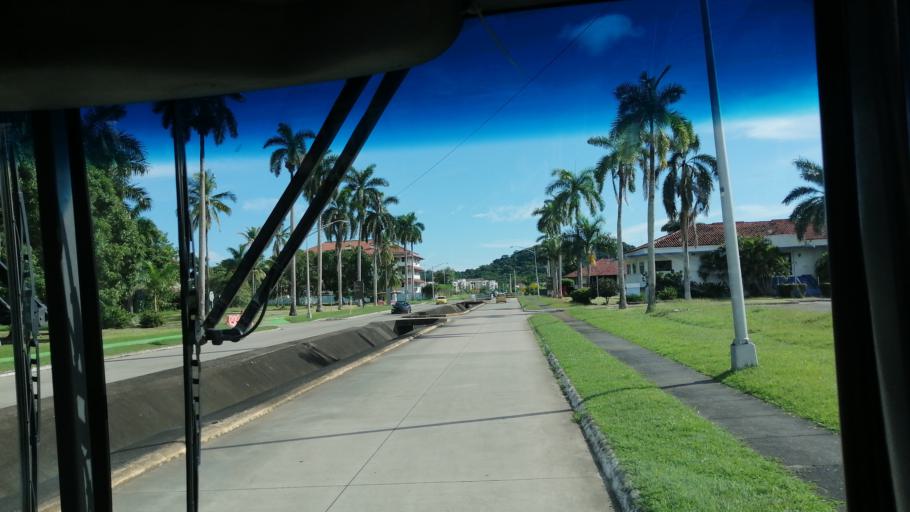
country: PA
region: Panama
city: Veracruz
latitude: 8.9128
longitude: -79.5920
